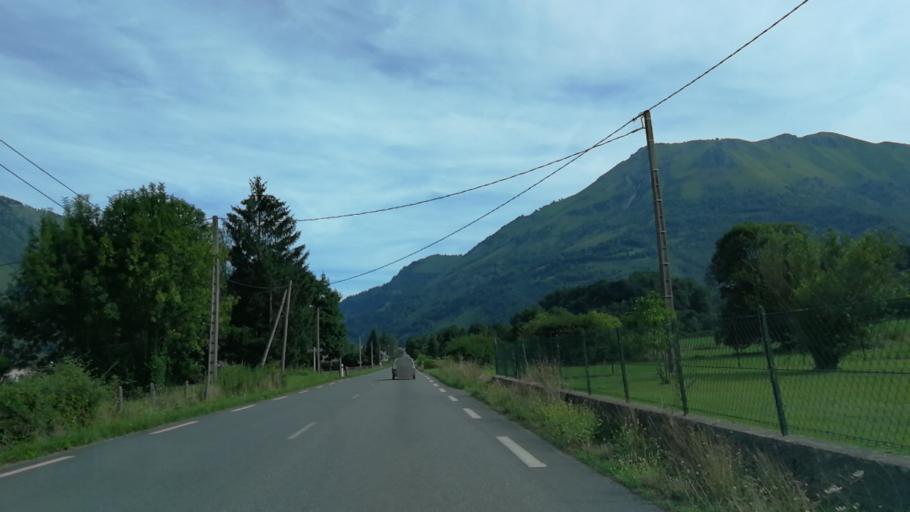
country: FR
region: Aquitaine
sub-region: Departement des Pyrenees-Atlantiques
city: Arette
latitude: 42.9809
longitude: -0.6057
